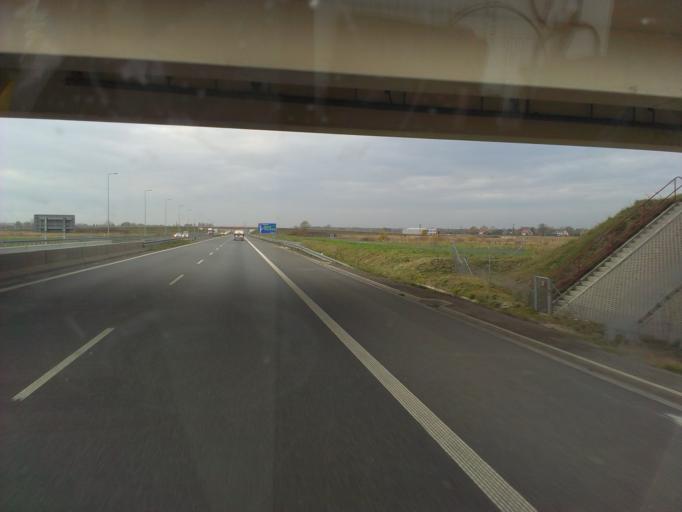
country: PL
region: Lesser Poland Voivodeship
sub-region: Powiat bochenski
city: Krzeczow
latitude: 50.0028
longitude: 20.4706
